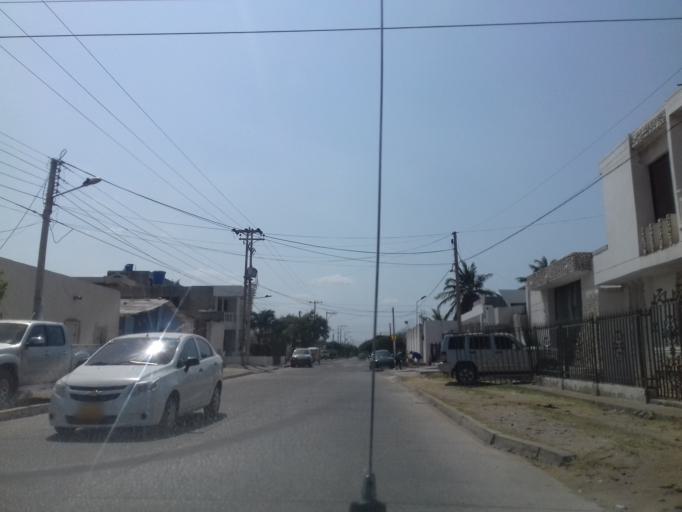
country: CO
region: La Guajira
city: Maicao
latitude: 11.3823
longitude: -72.2454
